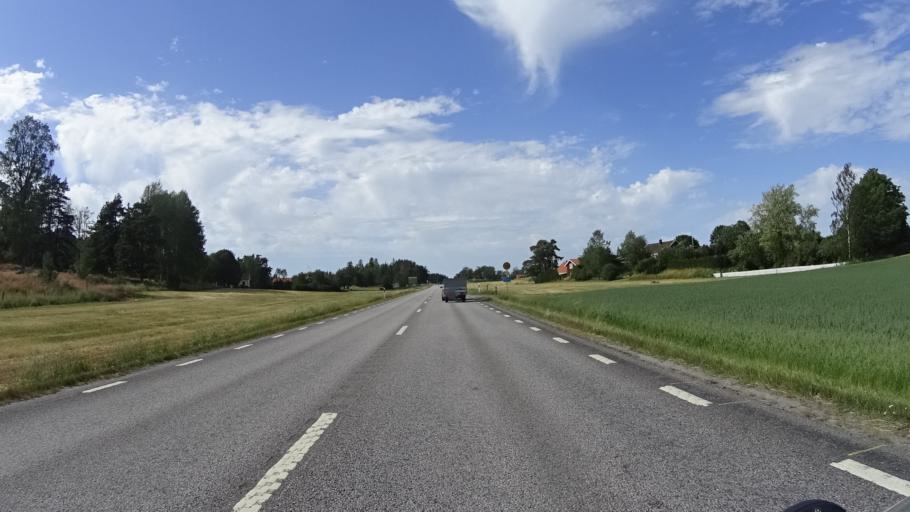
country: SE
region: OEstergoetland
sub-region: Linkopings Kommun
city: Linghem
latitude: 58.3506
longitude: 15.8373
